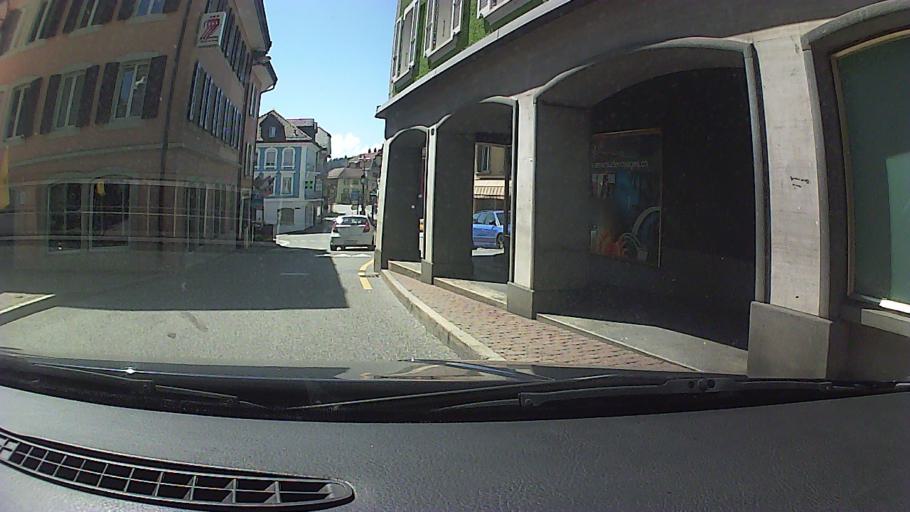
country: CH
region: Fribourg
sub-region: Veveyse District
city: Chatel-Saint-Denis
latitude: 46.5273
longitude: 6.9012
